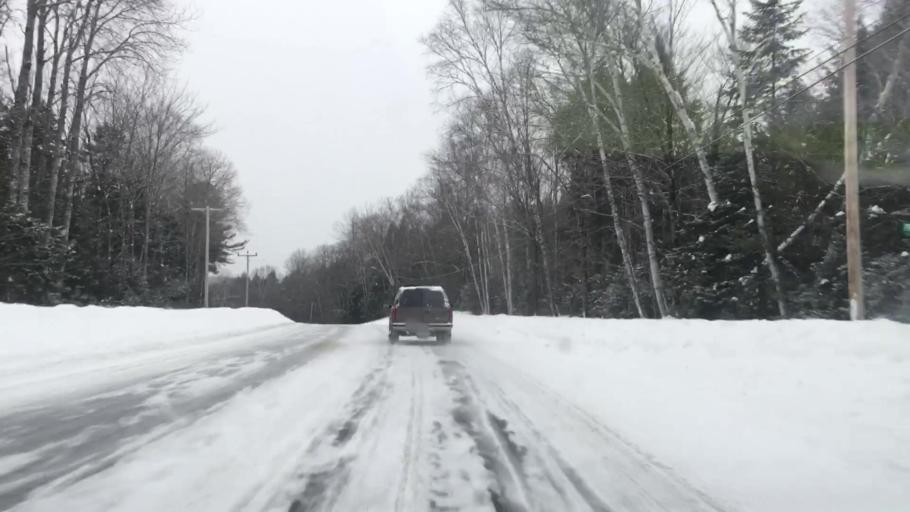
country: US
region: Maine
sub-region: Penobscot County
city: Medway
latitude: 45.5994
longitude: -68.4614
